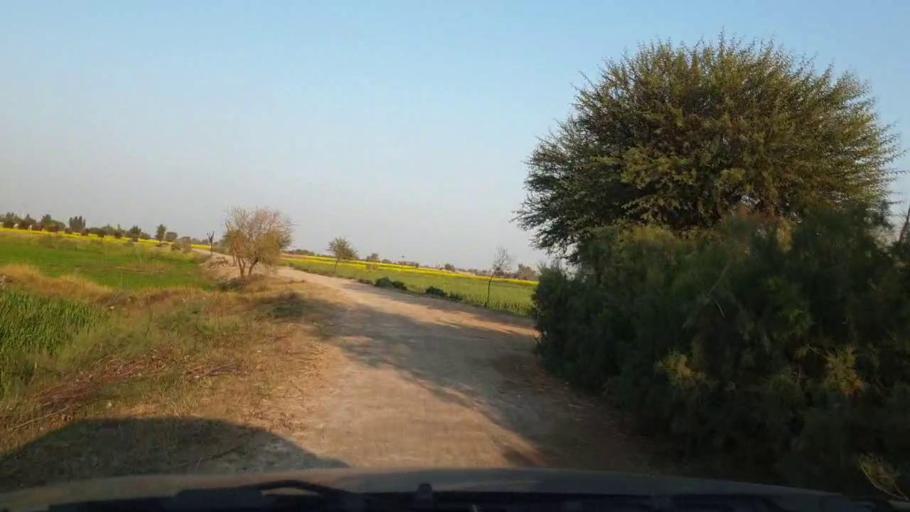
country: PK
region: Sindh
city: Jhol
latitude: 25.9324
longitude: 68.9314
